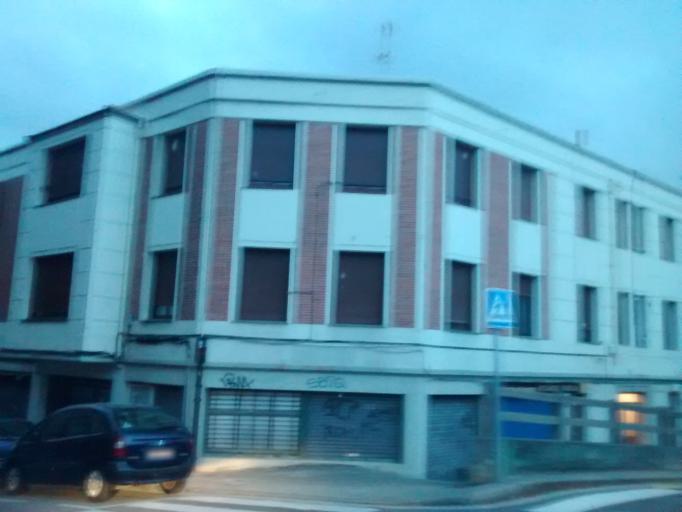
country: ES
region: Basque Country
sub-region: Bizkaia
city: Bilbao
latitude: 43.2640
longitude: -2.9158
